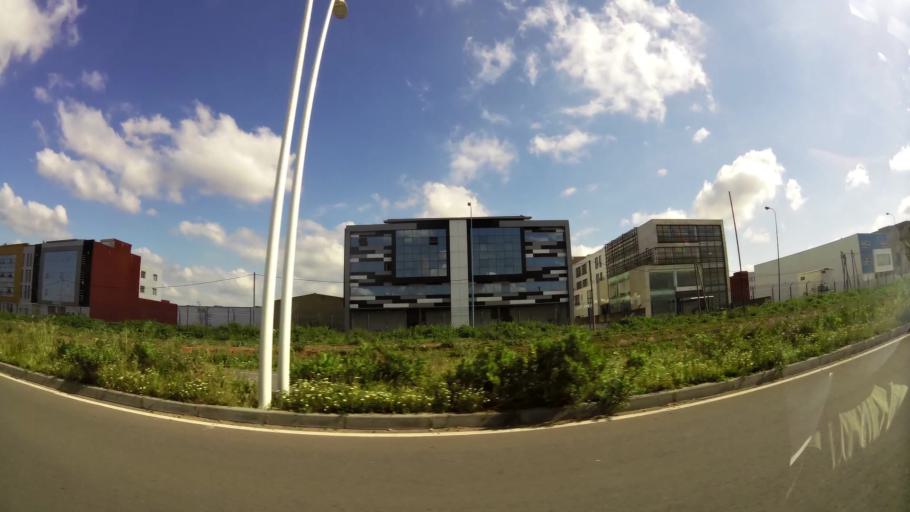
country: MA
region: Grand Casablanca
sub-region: Mediouna
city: Mediouna
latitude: 33.4067
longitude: -7.5500
